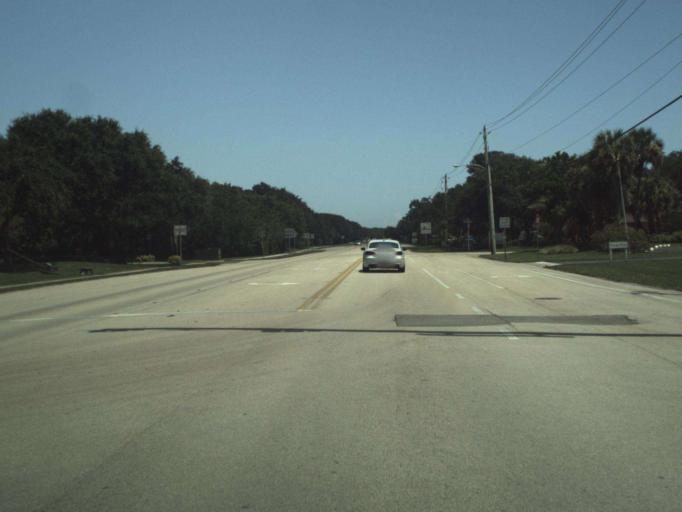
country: US
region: Florida
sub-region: Indian River County
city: Indian River Shores
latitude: 27.6921
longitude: -80.3710
